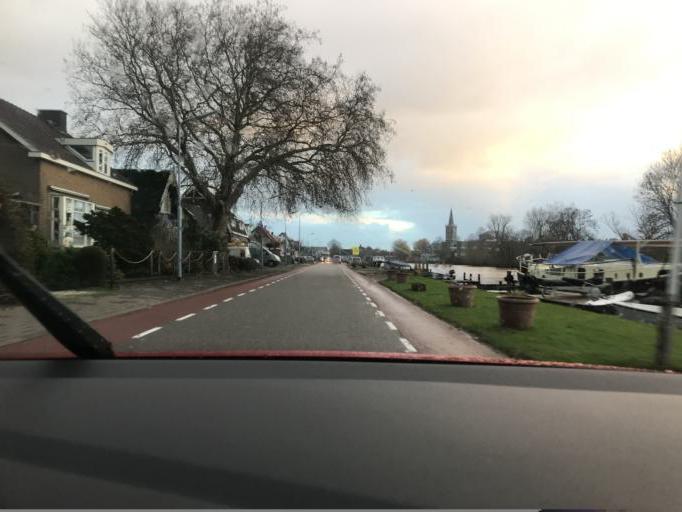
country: NL
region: North Holland
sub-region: Gemeente Aalsmeer
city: Aalsmeer
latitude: 52.2688
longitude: 4.7407
